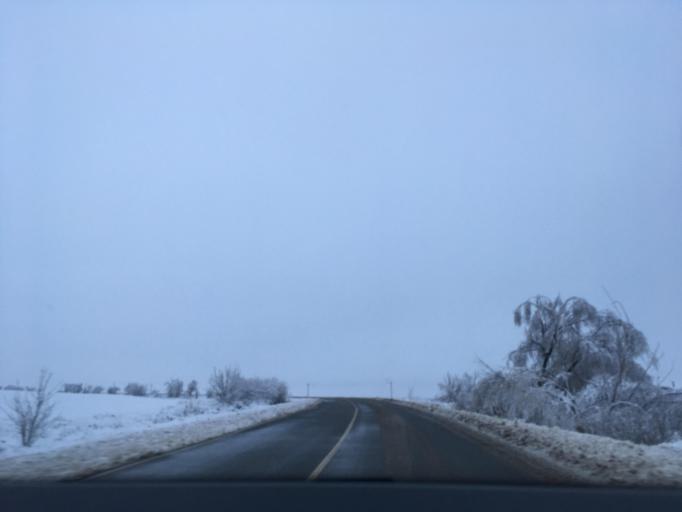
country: RU
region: Voronezj
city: Verkhniy Mamon
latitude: 50.0256
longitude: 40.0726
